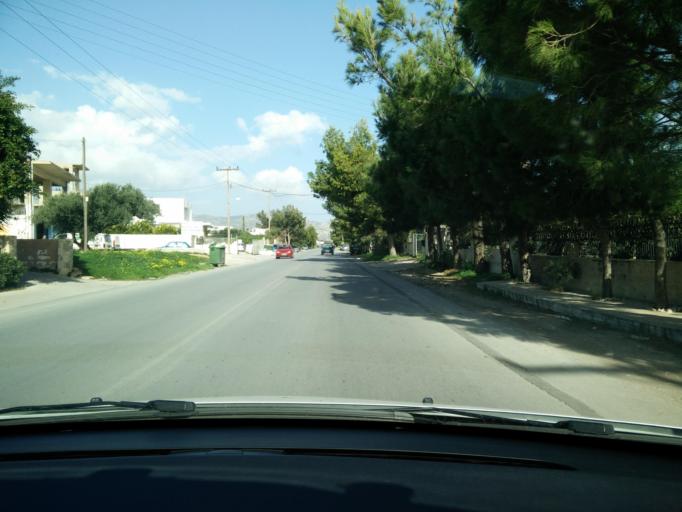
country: GR
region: Crete
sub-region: Nomos Lasithiou
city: Ierapetra
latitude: 35.0197
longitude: 25.7489
